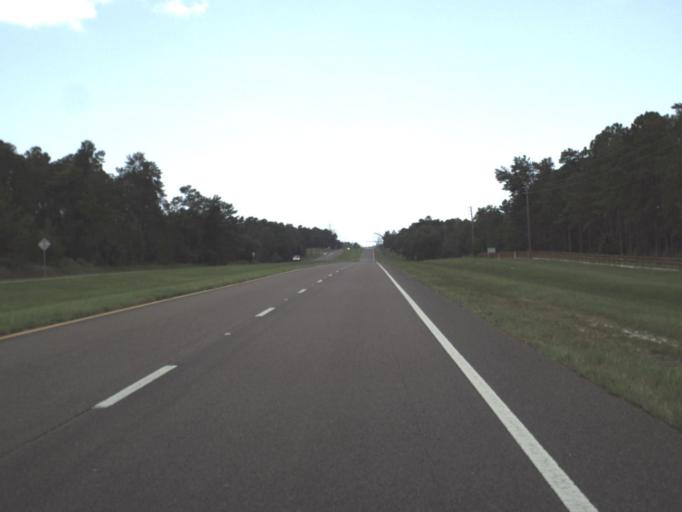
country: US
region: Florida
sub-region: Citrus County
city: Sugarmill Woods
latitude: 28.6793
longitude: -82.4875
